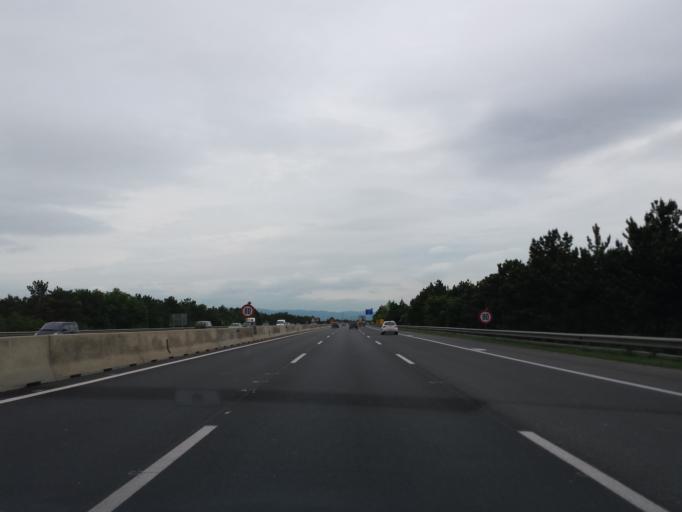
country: AT
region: Lower Austria
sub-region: Politischer Bezirk Wiener Neustadt
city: Weikersdorf am Steinfelde
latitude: 47.8134
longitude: 16.1943
